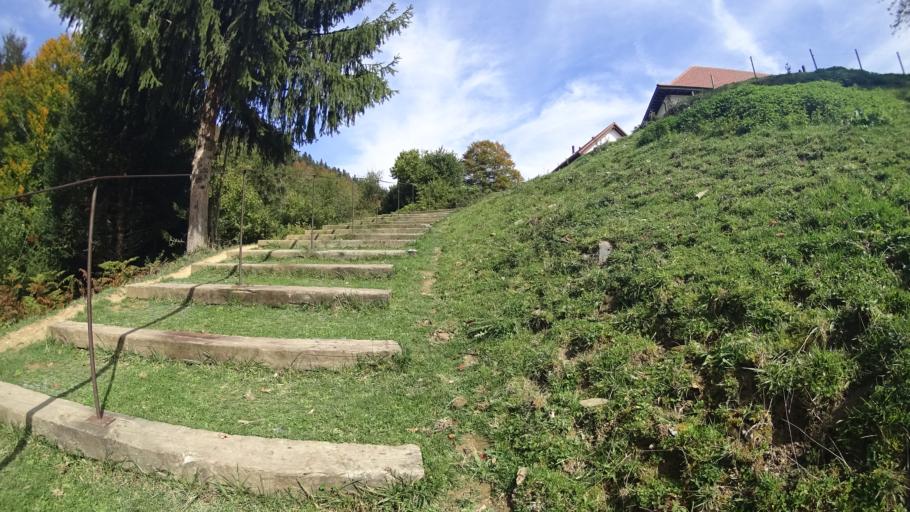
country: ES
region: Navarre
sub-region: Provincia de Navarra
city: Oronz
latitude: 42.9888
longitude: -1.1056
